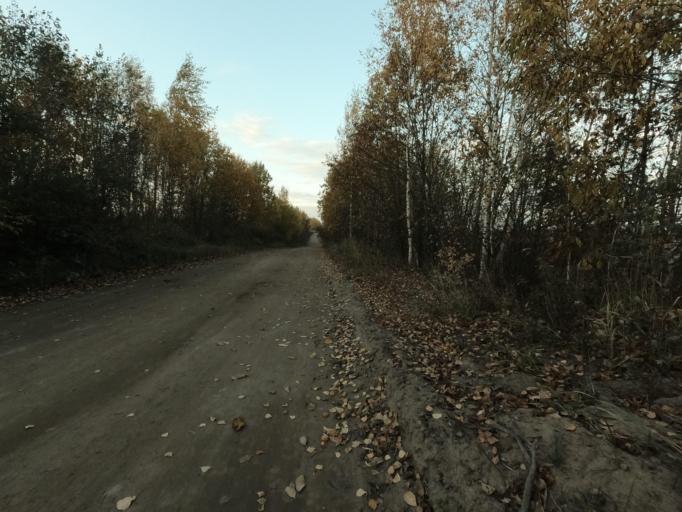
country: RU
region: Leningrad
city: Mga
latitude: 59.7903
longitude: 31.2016
